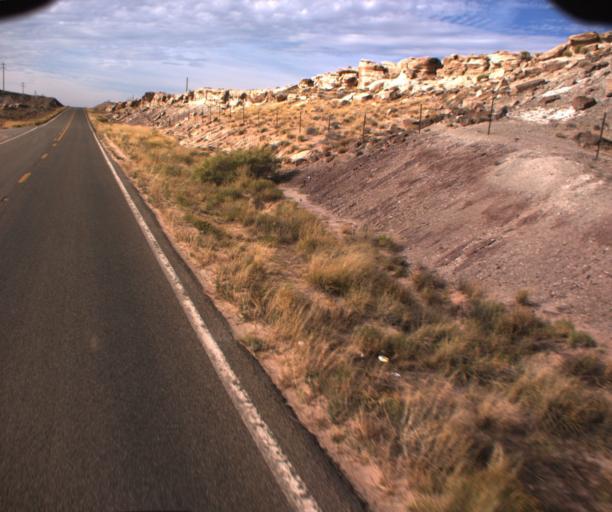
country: US
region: Arizona
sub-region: Apache County
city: Many Farms
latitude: 36.4917
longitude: -109.4951
